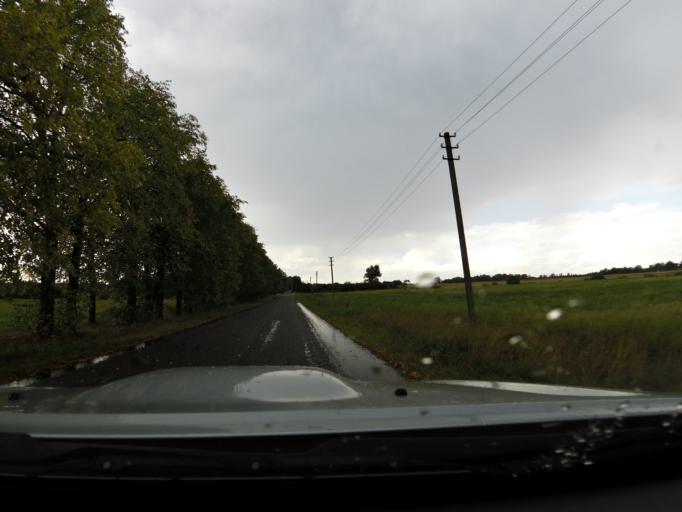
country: LT
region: Vilnius County
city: Ukmerge
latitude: 55.2814
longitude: 24.5482
